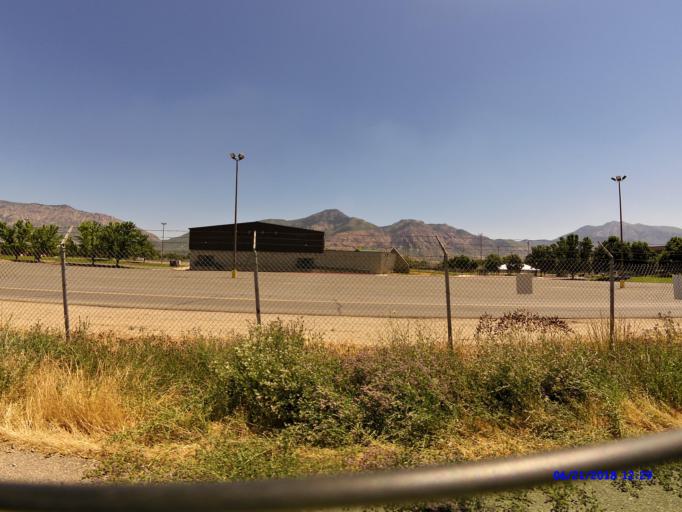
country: US
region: Utah
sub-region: Weber County
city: Harrisville
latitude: 41.2770
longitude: -111.9999
